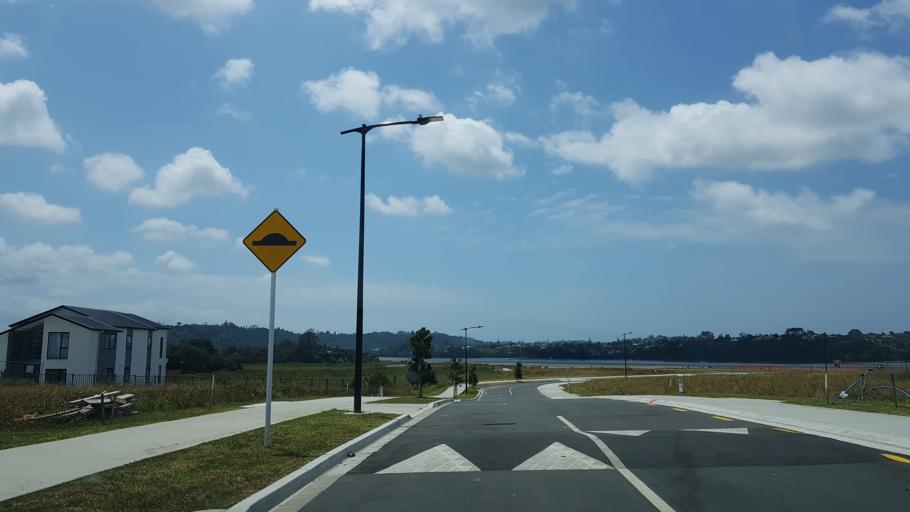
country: NZ
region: Auckland
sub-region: Auckland
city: Rosebank
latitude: -36.8029
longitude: 174.6697
